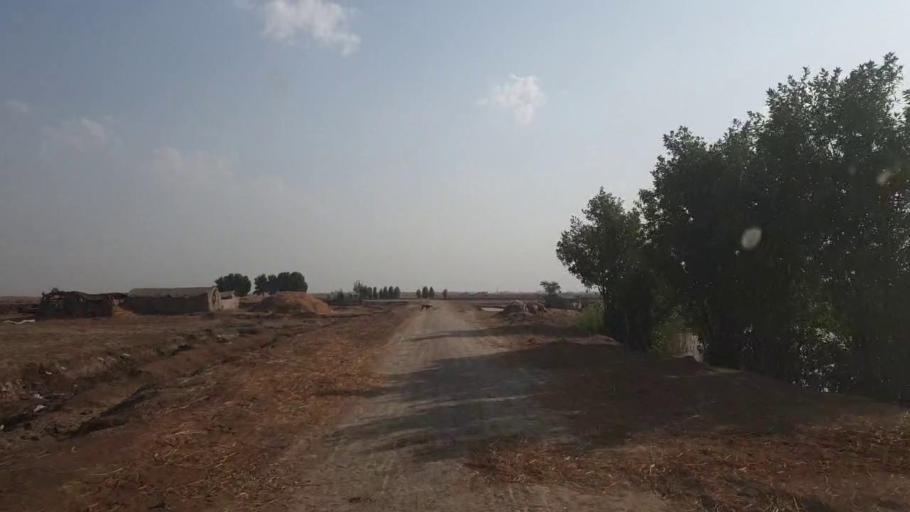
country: PK
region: Sindh
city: Kario
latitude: 24.5789
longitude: 68.5416
